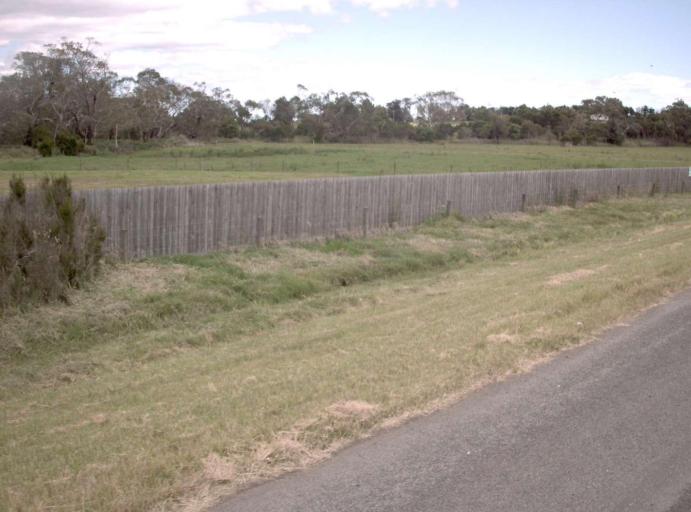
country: AU
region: Victoria
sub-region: Cardinia
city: Koo-Wee-Rup
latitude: -38.3247
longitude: 145.5431
